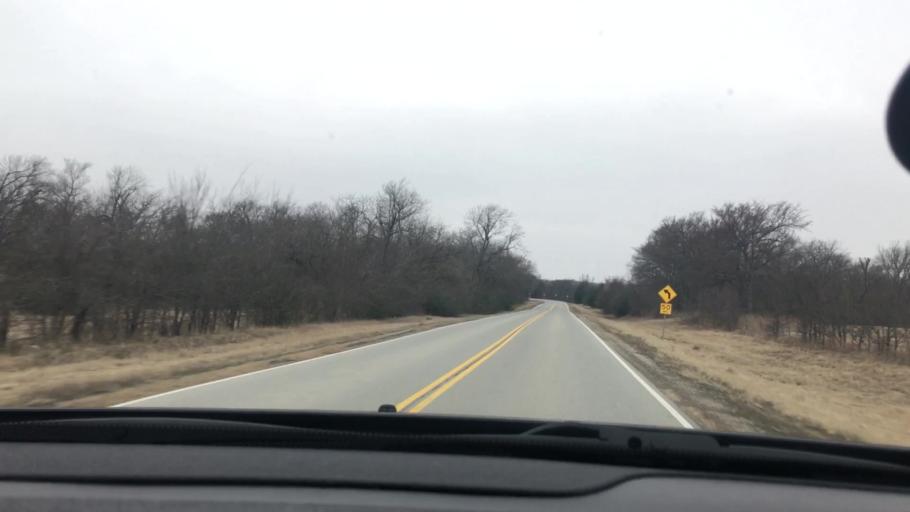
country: US
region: Oklahoma
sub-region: Coal County
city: Coalgate
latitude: 34.5313
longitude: -96.2580
